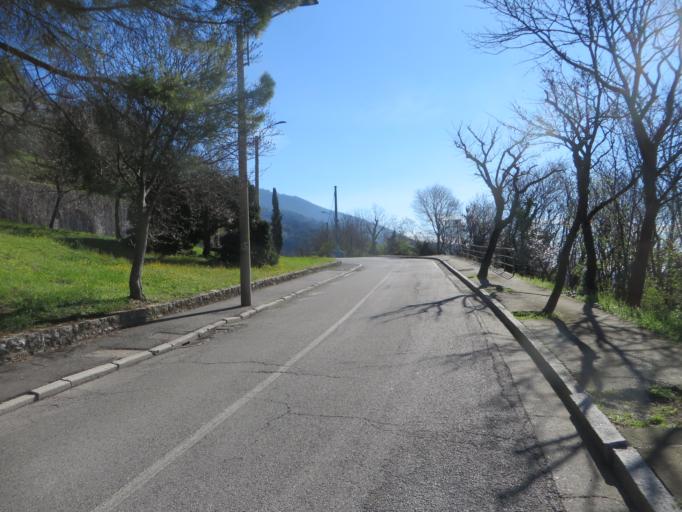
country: IT
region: Lombardy
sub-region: Provincia di Brescia
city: Brescia
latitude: 45.5376
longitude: 10.2392
